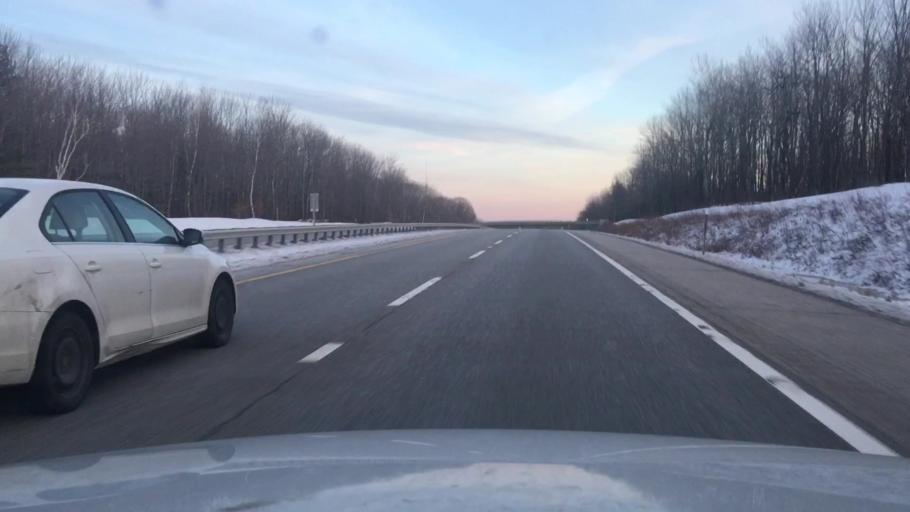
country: US
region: Maine
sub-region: Androscoggin County
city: Sabattus
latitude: 44.1250
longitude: -69.9851
